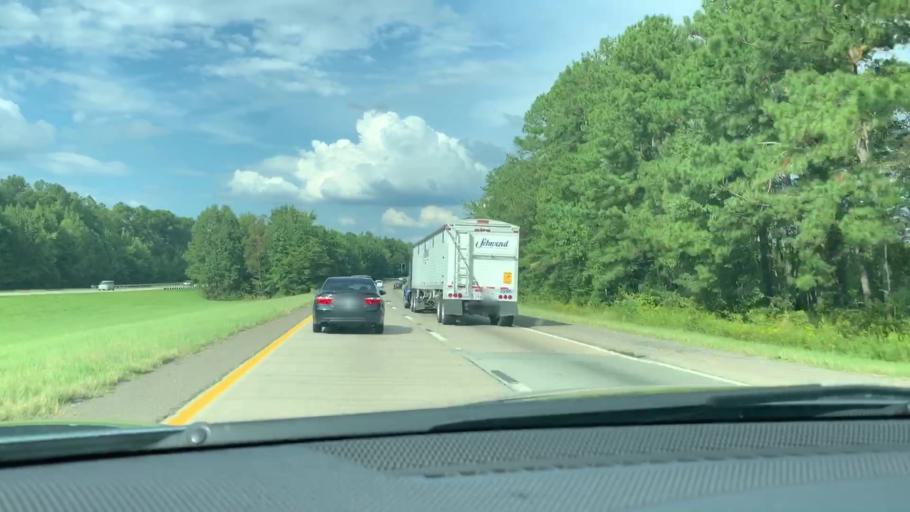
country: US
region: South Carolina
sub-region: Hampton County
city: Yemassee
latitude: 32.6888
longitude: -80.8805
